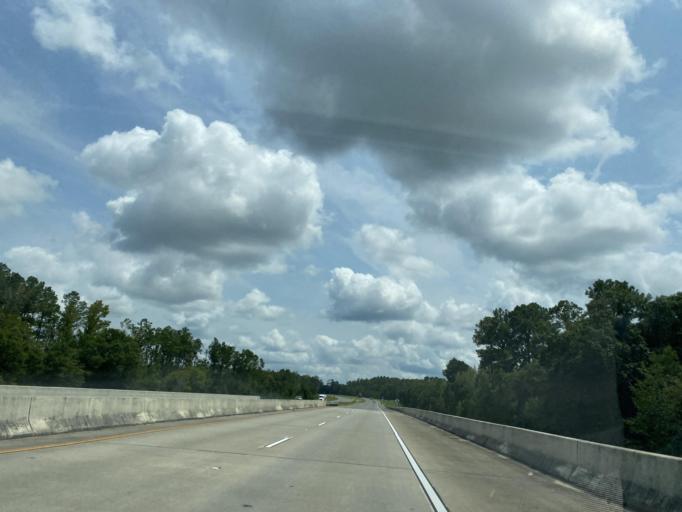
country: US
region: Georgia
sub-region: Ware County
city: Deenwood
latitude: 31.2996
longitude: -82.4529
